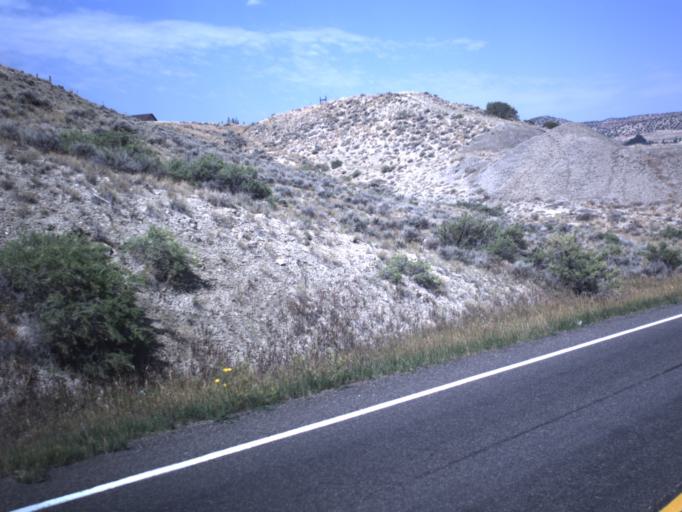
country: US
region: Utah
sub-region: Daggett County
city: Manila
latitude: 40.9708
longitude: -109.7158
